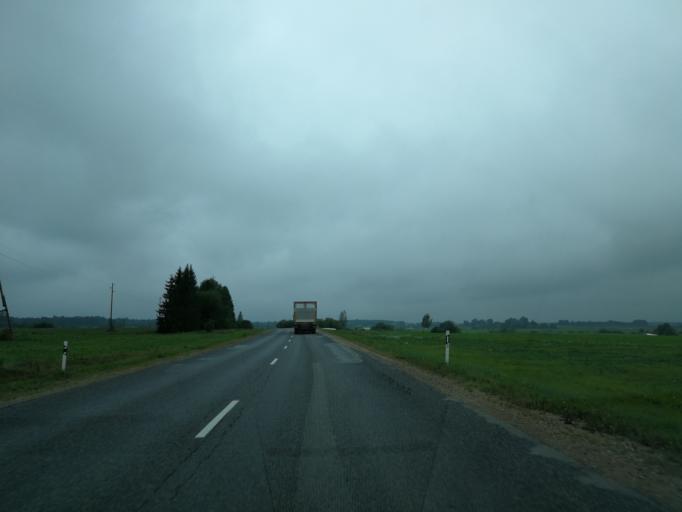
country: LV
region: Livani
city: Livani
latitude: 56.3539
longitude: 26.2449
